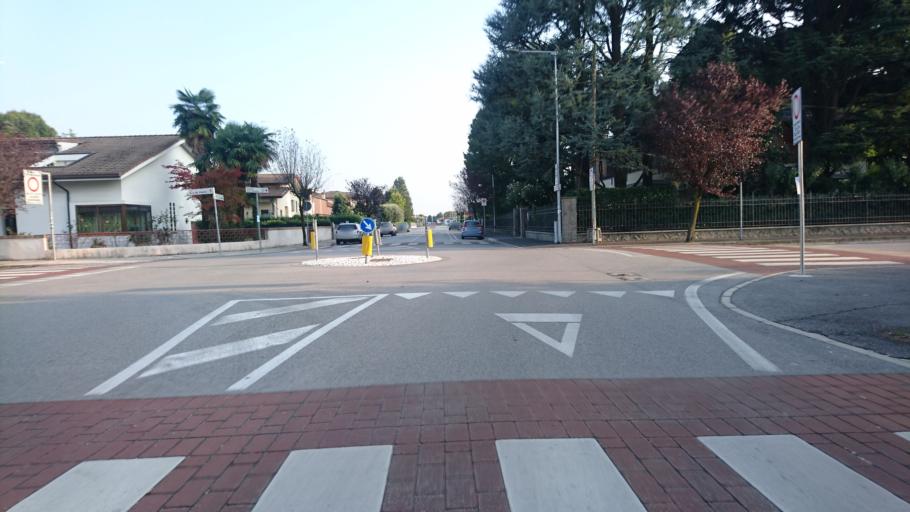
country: IT
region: Veneto
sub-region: Provincia di Padova
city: Limena
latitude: 45.4729
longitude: 11.8428
